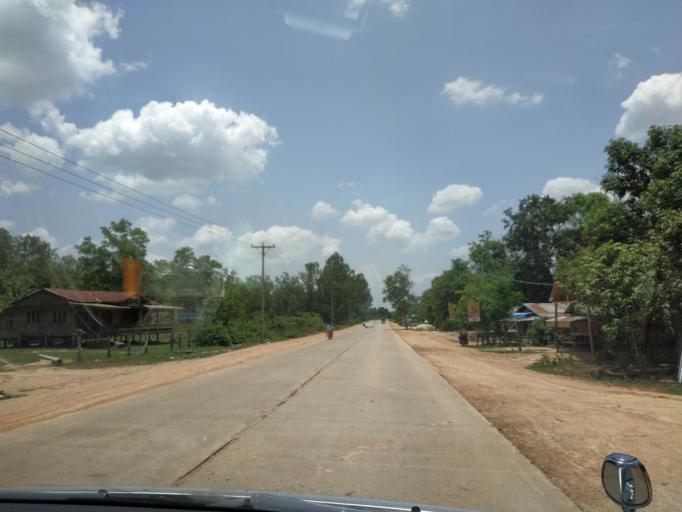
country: MM
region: Bago
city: Bago
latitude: 17.4715
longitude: 96.4707
